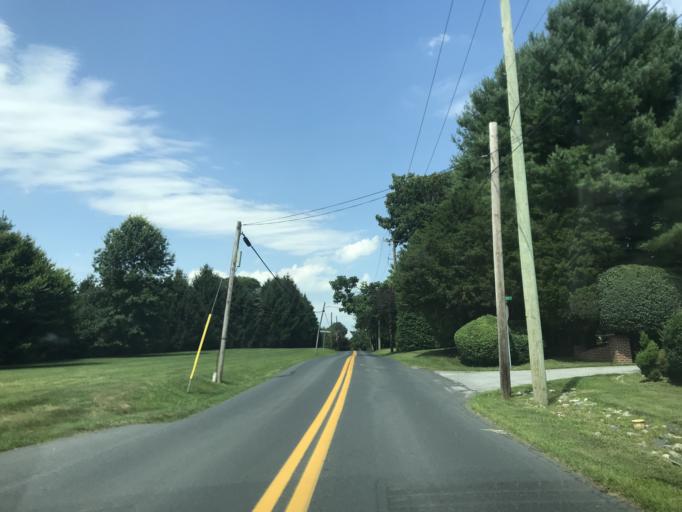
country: US
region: Delaware
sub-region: New Castle County
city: Greenville
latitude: 39.8179
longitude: -75.6204
